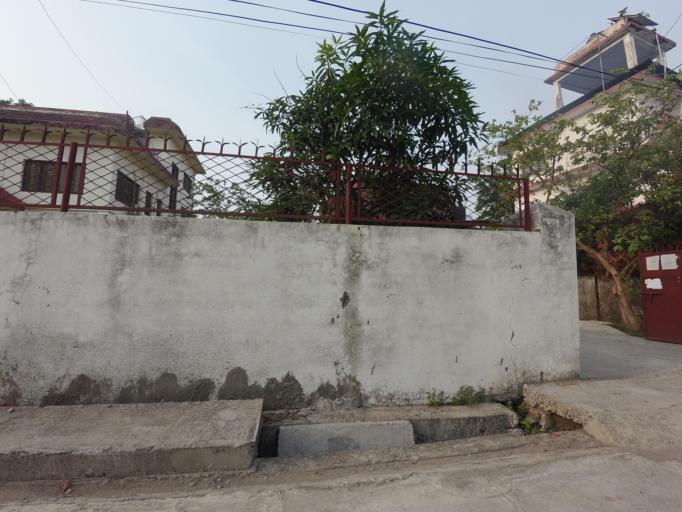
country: NP
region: Western Region
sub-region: Lumbini Zone
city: Bhairahawa
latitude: 27.5139
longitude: 83.4557
